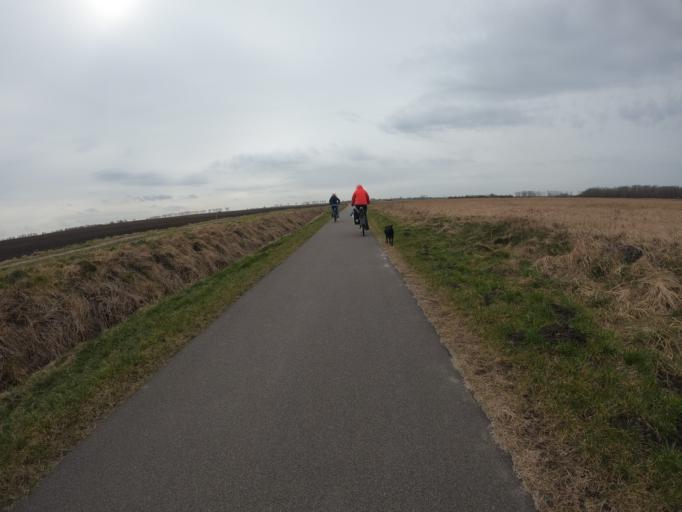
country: PL
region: West Pomeranian Voivodeship
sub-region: Powiat gryficki
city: Mrzezyno
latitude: 54.1087
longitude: 15.2938
